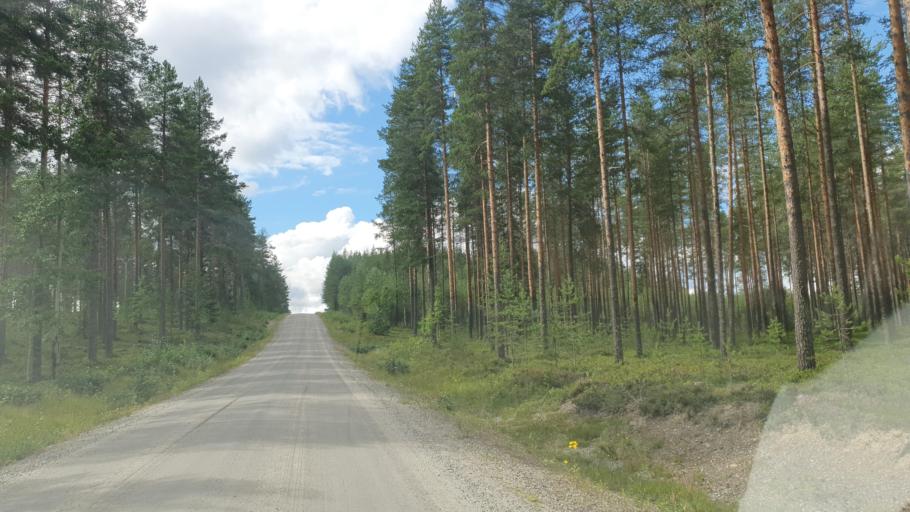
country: FI
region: Kainuu
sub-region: Kehys-Kainuu
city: Kuhmo
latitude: 64.1079
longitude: 29.3469
